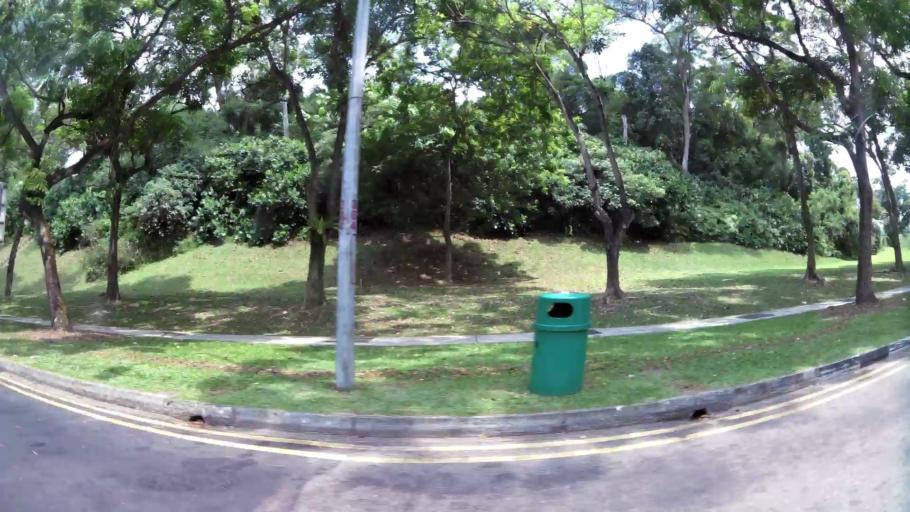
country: MY
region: Johor
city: Johor Bahru
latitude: 1.4276
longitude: 103.7627
